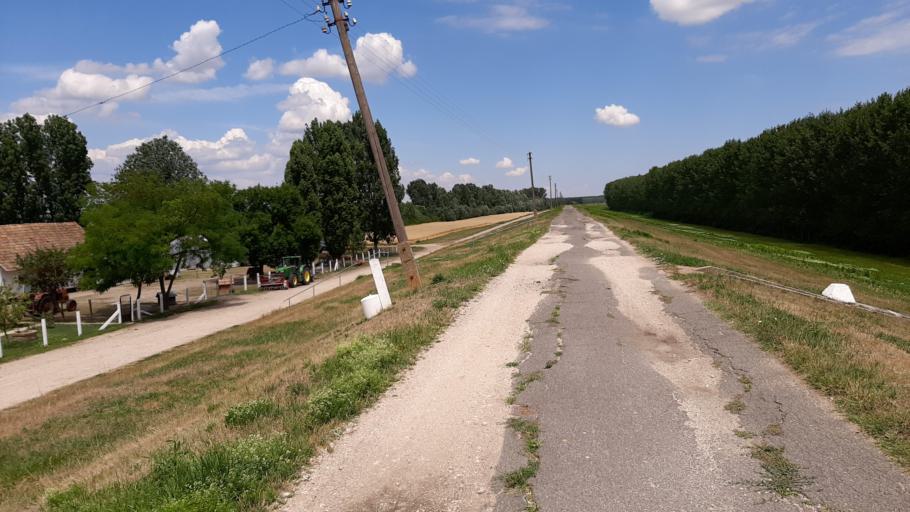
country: HU
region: Csongrad
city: Csongrad
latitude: 46.6519
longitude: 20.1841
